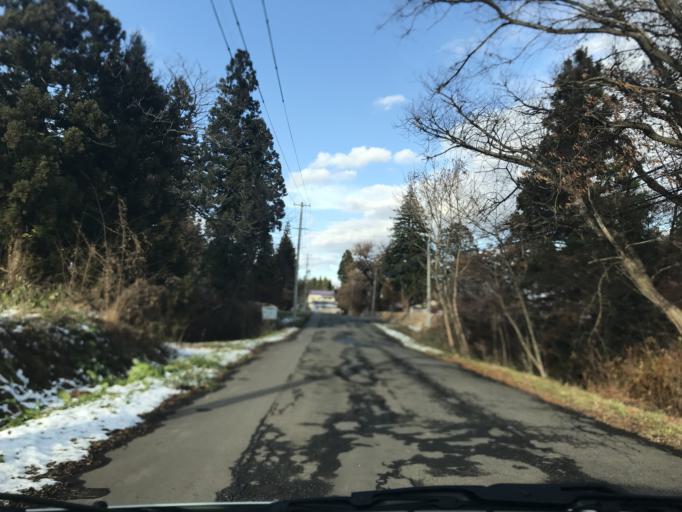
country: JP
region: Iwate
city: Kitakami
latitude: 39.2328
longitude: 141.0503
